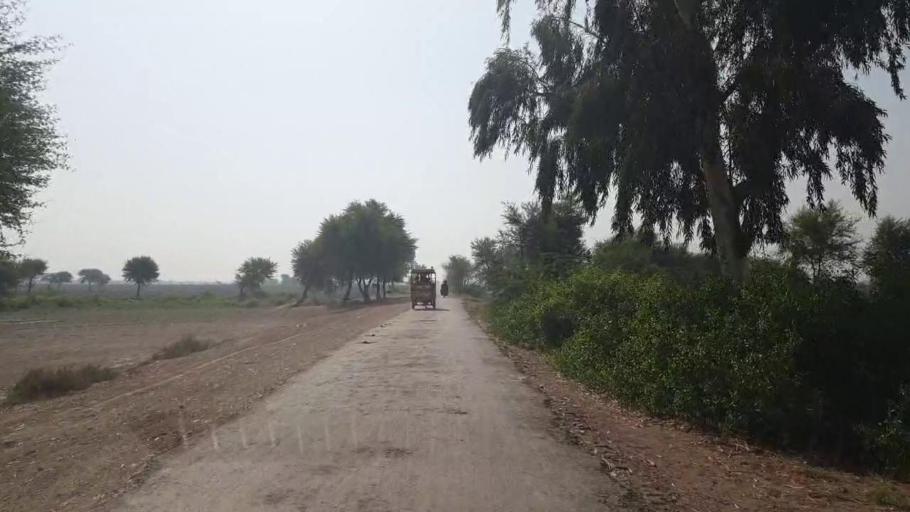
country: PK
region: Sindh
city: Shahdadpur
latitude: 25.9247
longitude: 68.7344
